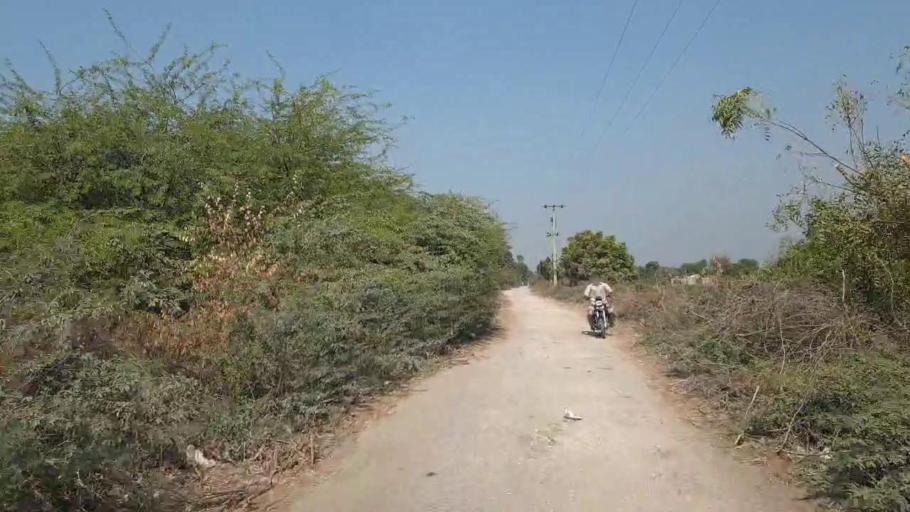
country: PK
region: Sindh
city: Chambar
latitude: 25.4079
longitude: 68.8958
